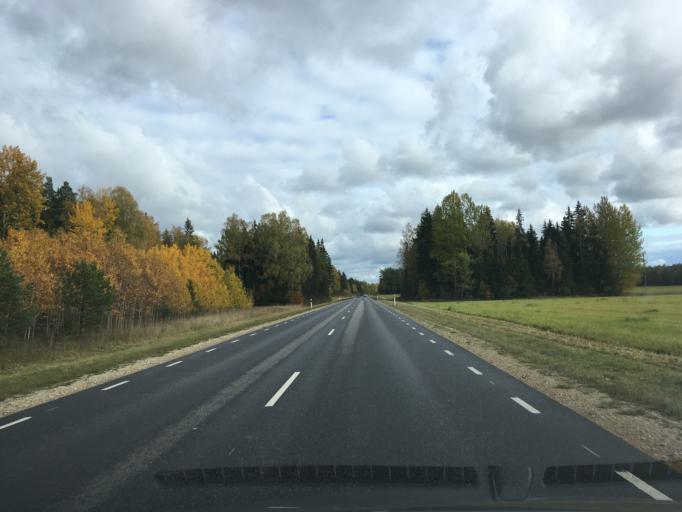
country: EE
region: Harju
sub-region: Anija vald
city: Kehra
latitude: 59.2174
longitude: 25.2309
